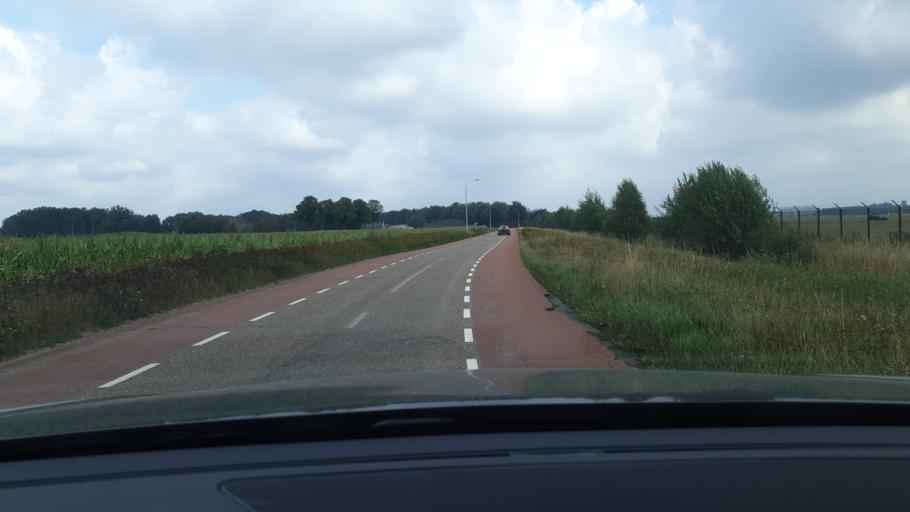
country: NL
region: North Brabant
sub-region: Gemeente Veldhoven
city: Oerle
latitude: 51.4400
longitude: 5.3577
